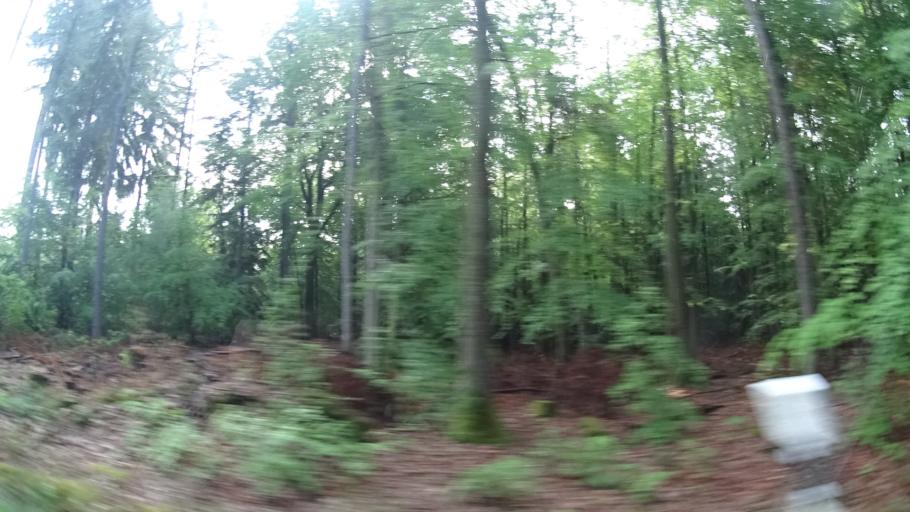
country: DE
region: Bavaria
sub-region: Regierungsbezirk Unterfranken
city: Laudenbach
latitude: 49.7420
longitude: 9.1157
